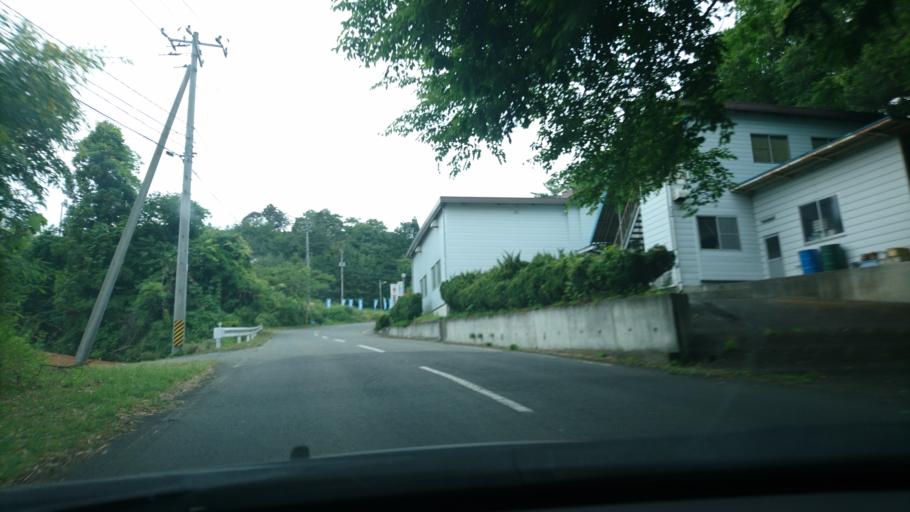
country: JP
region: Iwate
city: Ichinoseki
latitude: 38.9016
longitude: 141.1554
